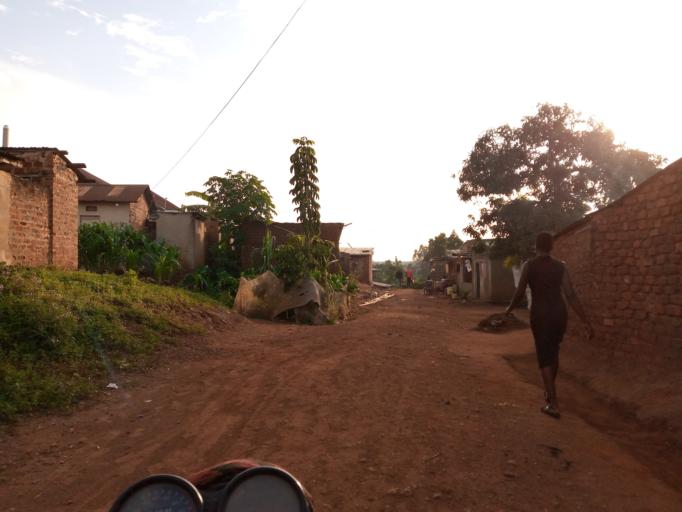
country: UG
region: Eastern Region
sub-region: Mbale District
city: Mbale
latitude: 1.0822
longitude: 34.1533
